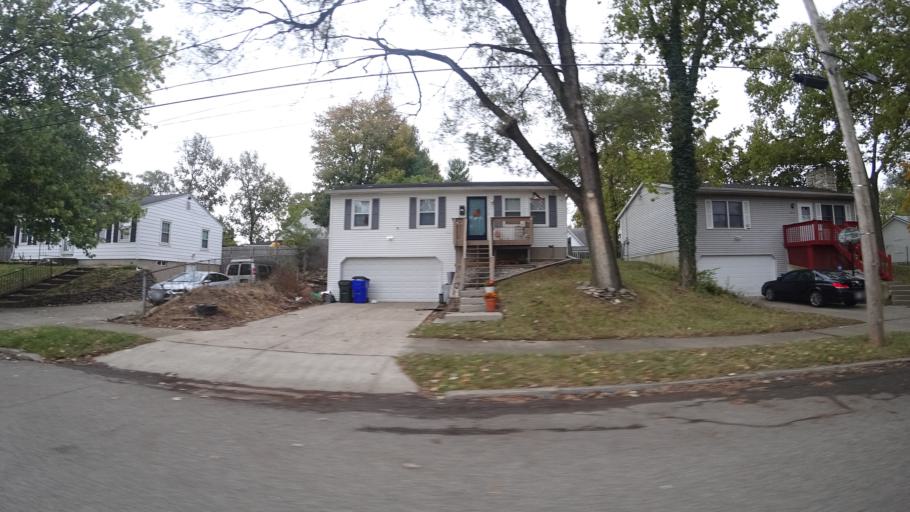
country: US
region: Ohio
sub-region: Butler County
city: Fairfield
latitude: 39.3682
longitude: -84.5589
